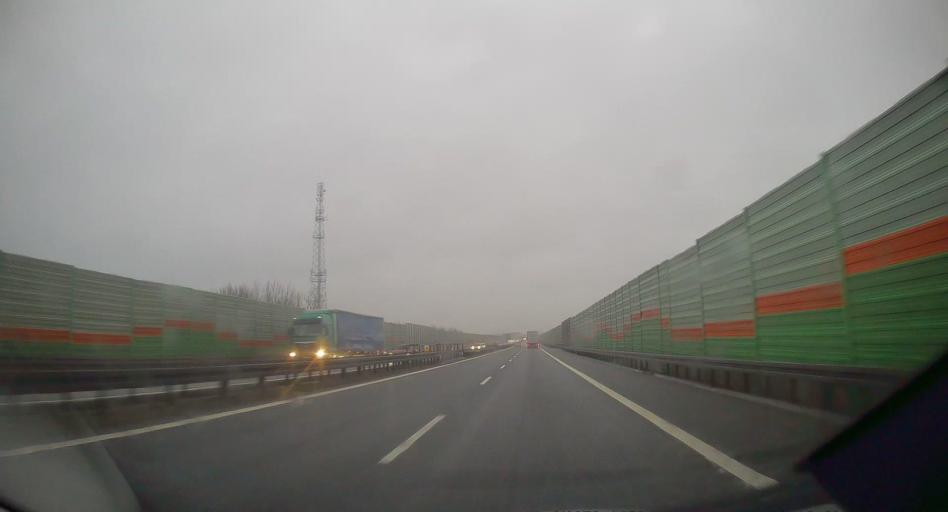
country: PL
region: Lodz Voivodeship
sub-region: Piotrkow Trybunalski
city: Piotrkow Trybunalski
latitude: 51.4433
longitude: 19.6952
